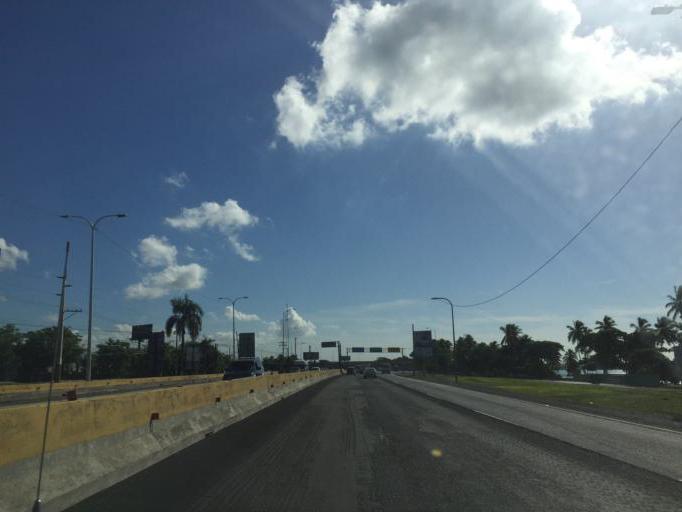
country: DO
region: Santo Domingo
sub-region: Santo Domingo
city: Boca Chica
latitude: 18.4543
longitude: -69.6951
